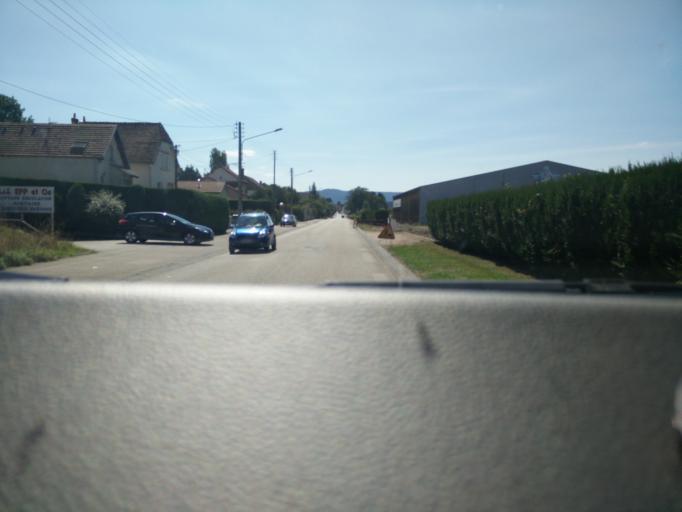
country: FR
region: Lorraine
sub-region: Departement des Vosges
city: Etival-Clairefontaine
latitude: 48.3703
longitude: 6.8775
